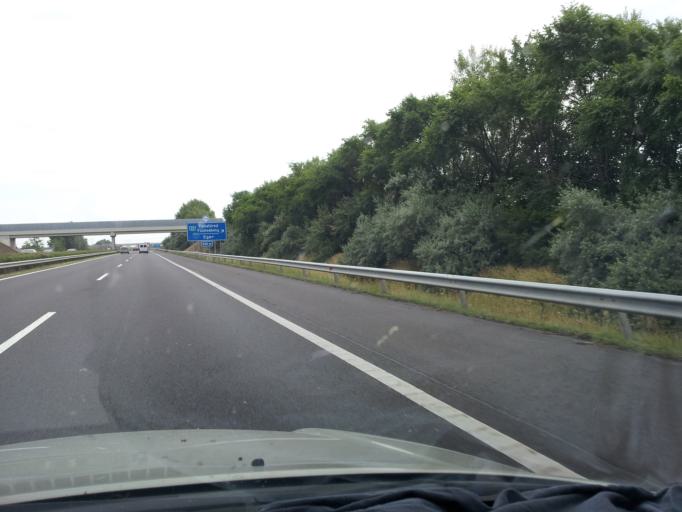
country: HU
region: Heves
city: Fuzesabony
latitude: 47.7304
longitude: 20.4025
